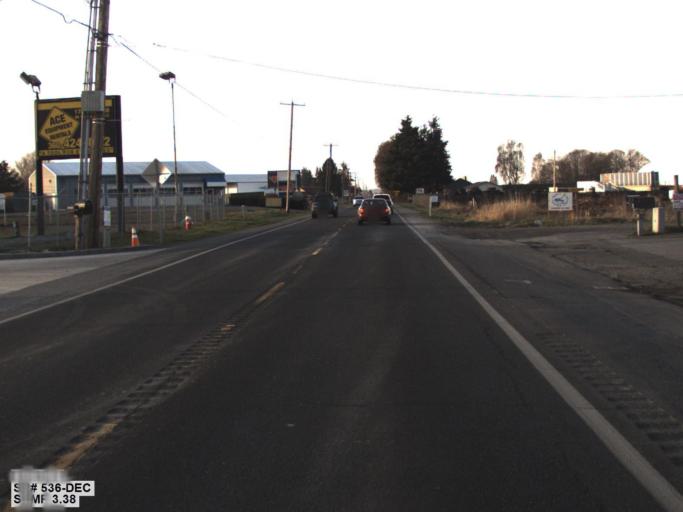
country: US
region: Washington
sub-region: Skagit County
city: Mount Vernon
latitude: 48.4300
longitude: -122.3662
